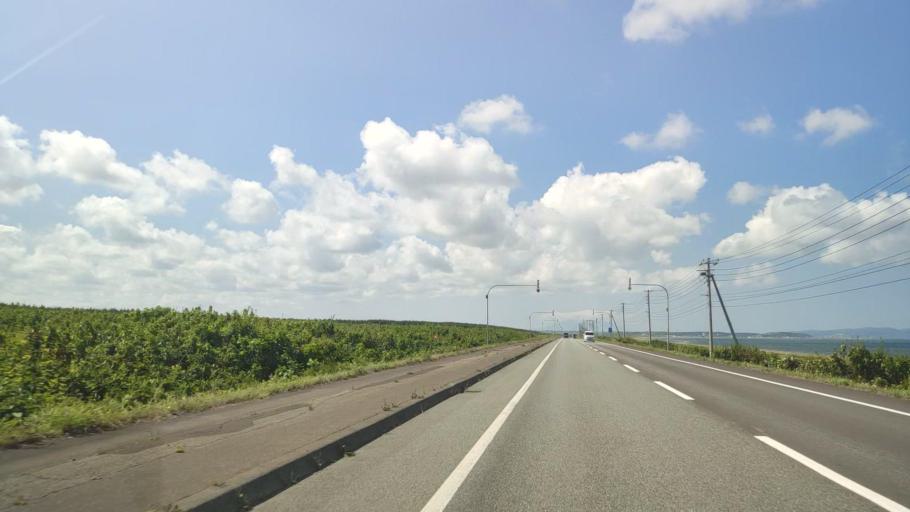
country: JP
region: Hokkaido
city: Makubetsu
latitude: 45.4177
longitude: 141.8318
